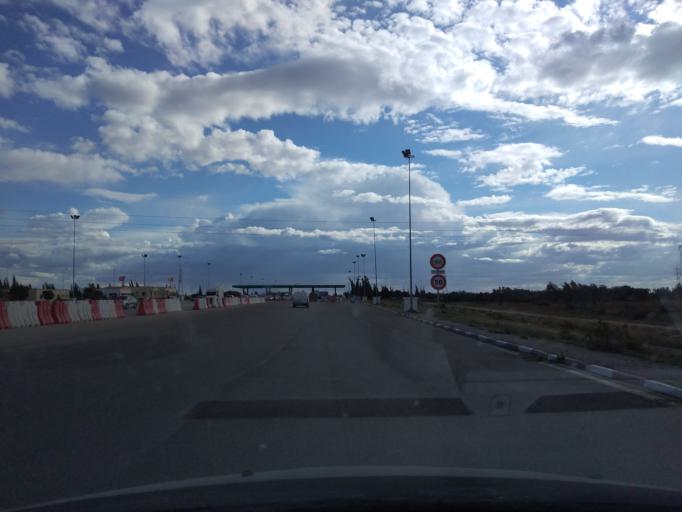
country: TN
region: Susah
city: Masakin
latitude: 35.6925
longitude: 10.5637
